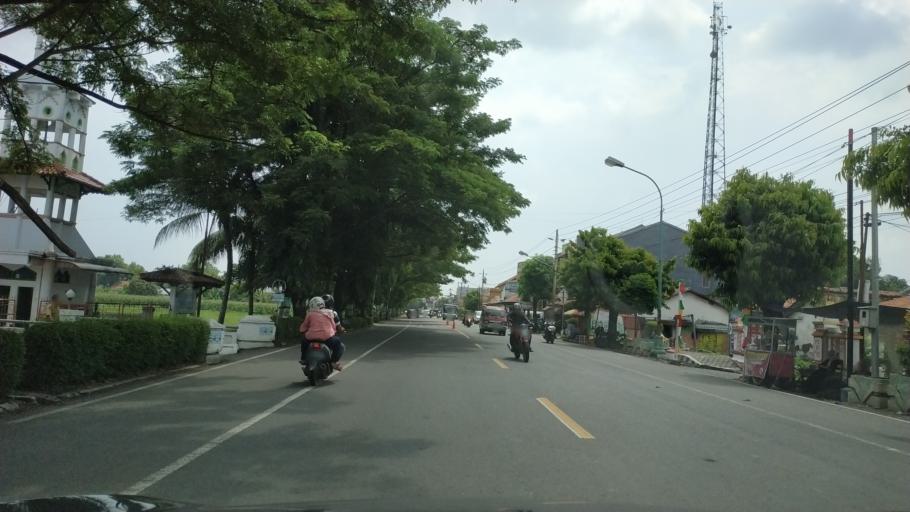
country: ID
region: Central Java
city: Slawi
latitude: -6.9949
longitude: 109.1416
